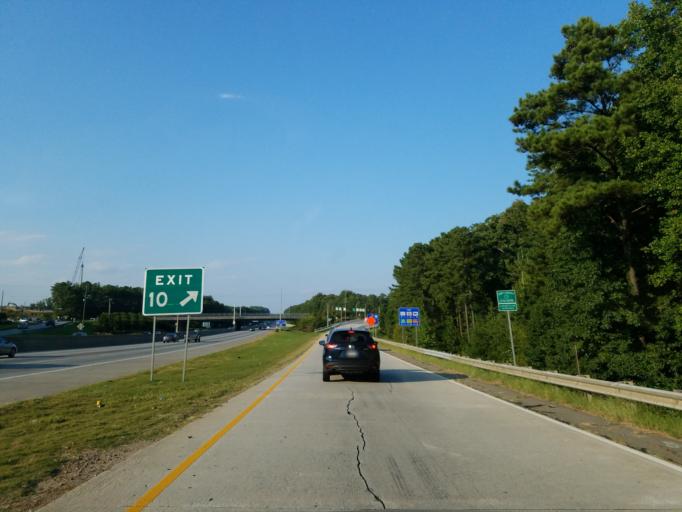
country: US
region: Georgia
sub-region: Fulton County
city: Alpharetta
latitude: 34.0661
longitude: -84.2730
